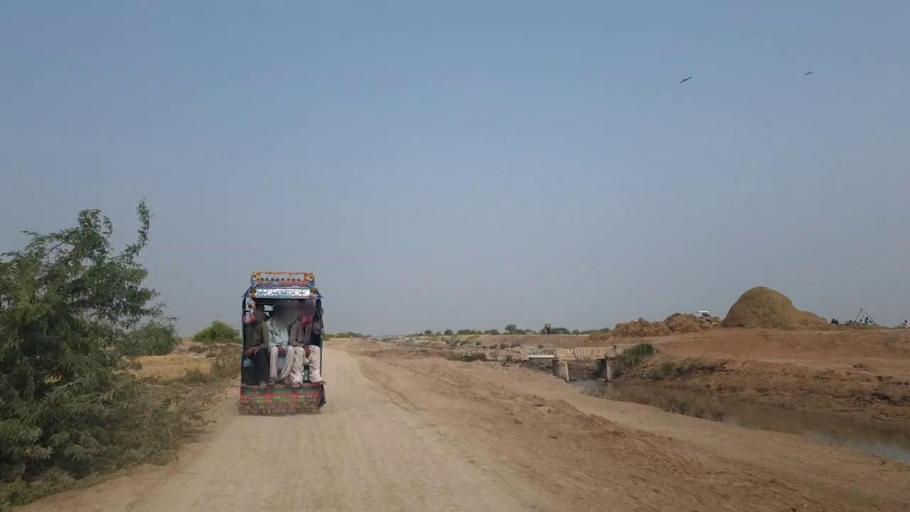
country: PK
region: Sindh
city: Badin
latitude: 24.7109
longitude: 68.7733
